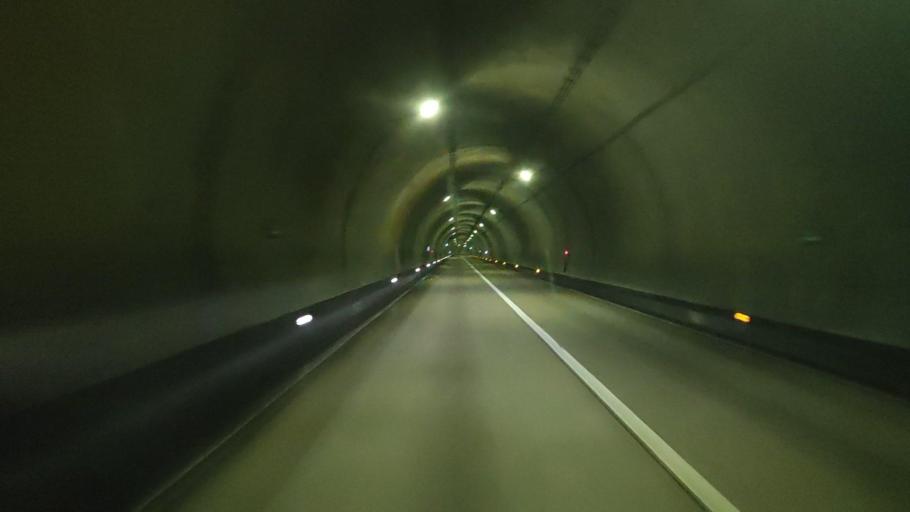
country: JP
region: Wakayama
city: Shingu
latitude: 33.8544
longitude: 135.8538
